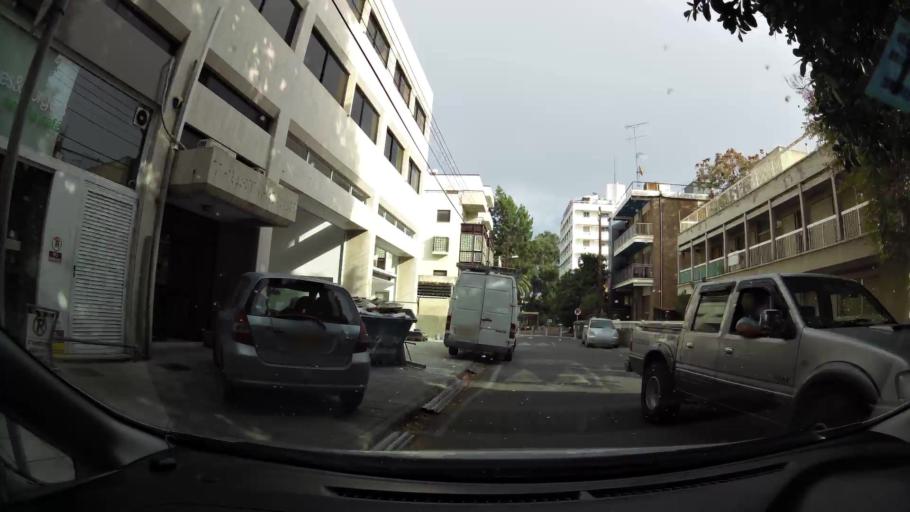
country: CY
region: Lefkosia
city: Nicosia
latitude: 35.1636
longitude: 33.3488
